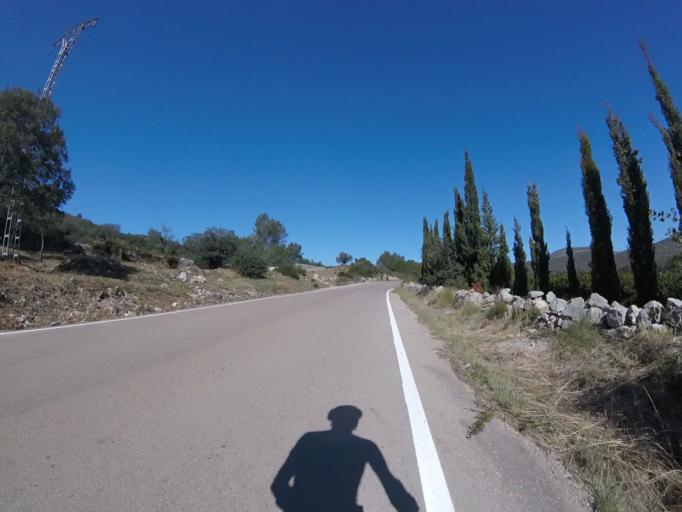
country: ES
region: Valencia
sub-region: Provincia de Castello
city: Santa Magdalena de Pulpis
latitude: 40.3669
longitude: 0.2759
